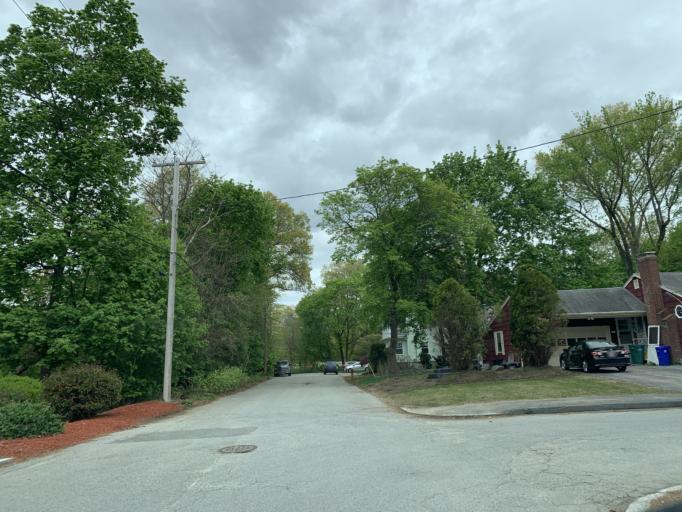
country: US
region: Massachusetts
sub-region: Bristol County
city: Attleboro
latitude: 41.9401
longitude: -71.2888
